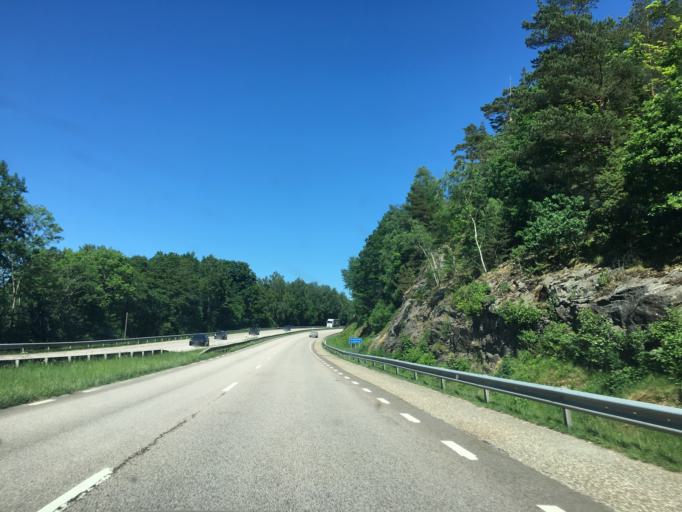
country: SE
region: Vaestra Goetaland
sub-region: Alingsas Kommun
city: Ingared
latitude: 57.8279
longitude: 12.4289
